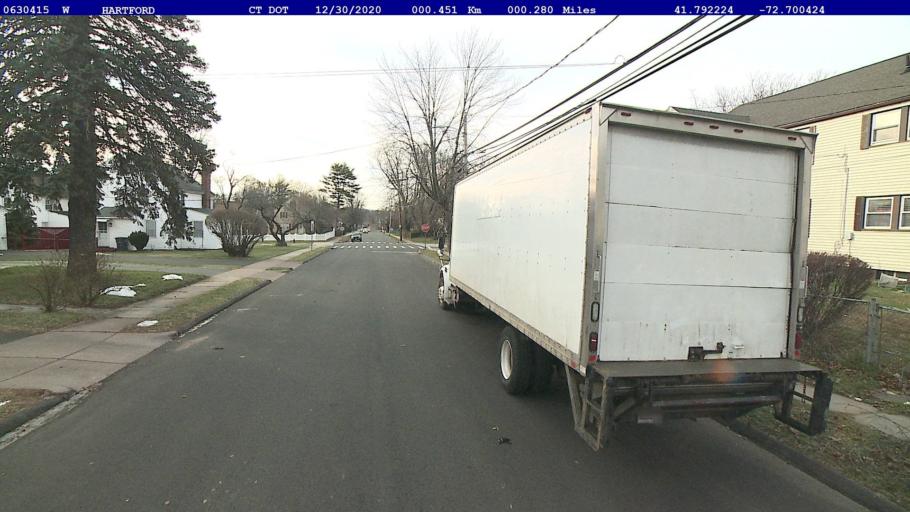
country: US
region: Connecticut
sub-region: Hartford County
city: Blue Hills
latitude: 41.7922
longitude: -72.7004
